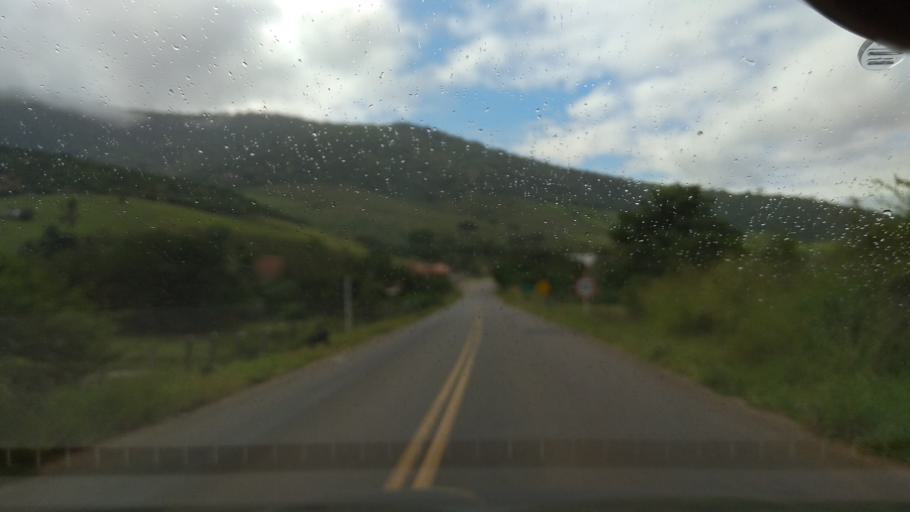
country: BR
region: Bahia
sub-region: Ubaira
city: Ubaira
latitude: -13.2511
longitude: -39.7182
